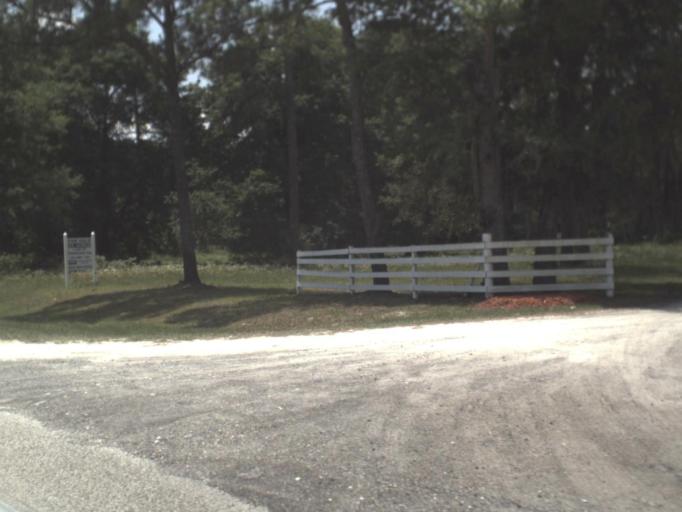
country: US
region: Florida
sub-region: Alachua County
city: Waldo
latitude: 29.8521
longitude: -82.1570
